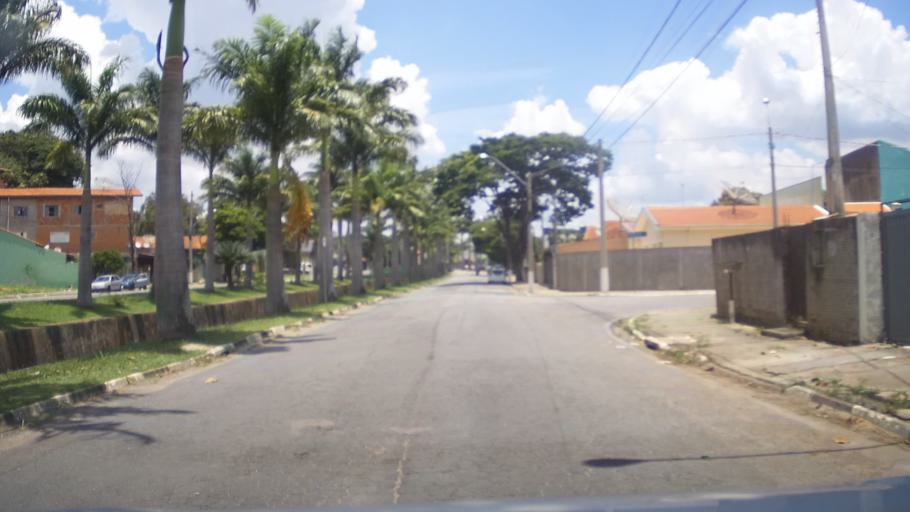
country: BR
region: Sao Paulo
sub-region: Vinhedo
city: Vinhedo
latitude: -23.0158
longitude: -46.9808
